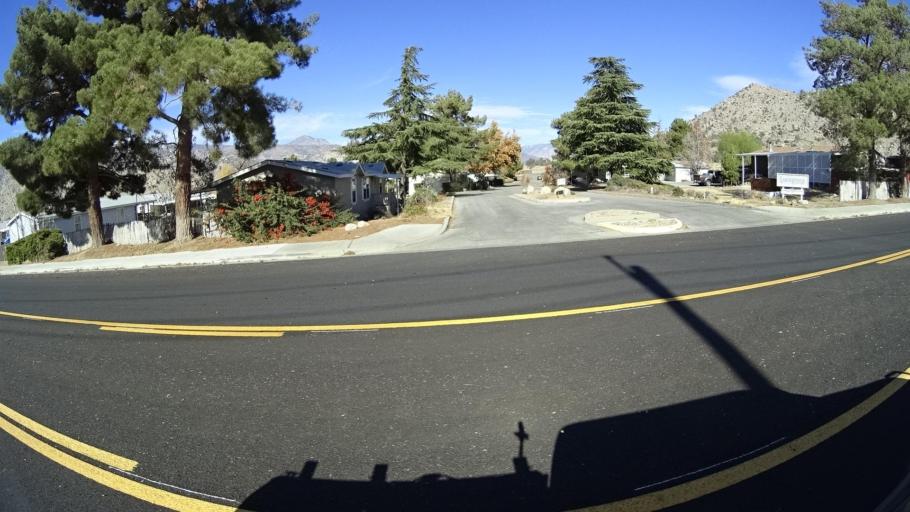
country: US
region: California
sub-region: Kern County
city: Lake Isabella
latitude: 35.6164
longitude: -118.4719
